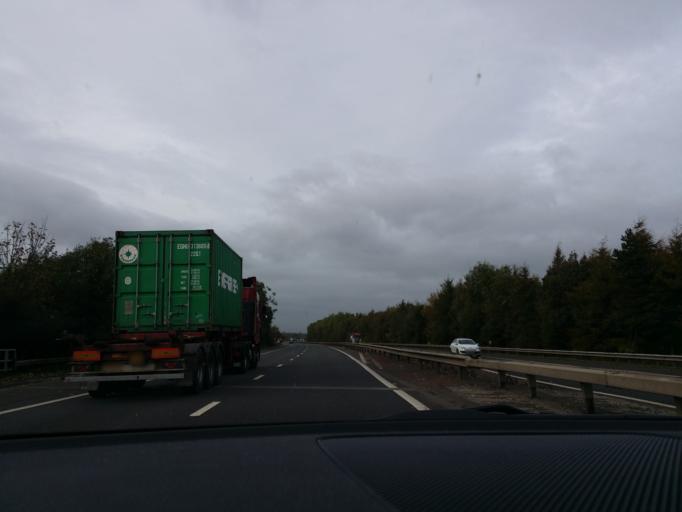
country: GB
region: Scotland
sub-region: Falkirk
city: Grangemouth
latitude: 56.0127
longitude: -3.7452
